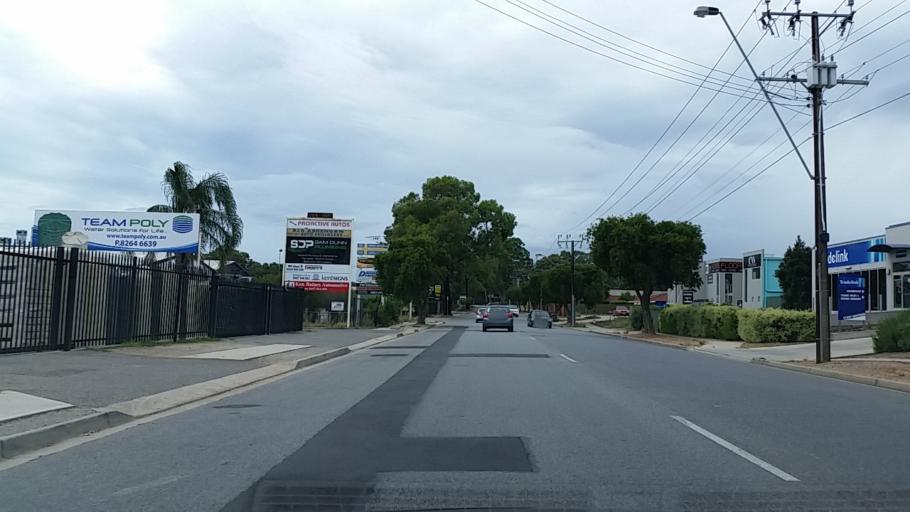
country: AU
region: South Australia
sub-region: Tea Tree Gully
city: Hope Valley
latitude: -34.8295
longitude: 138.7068
